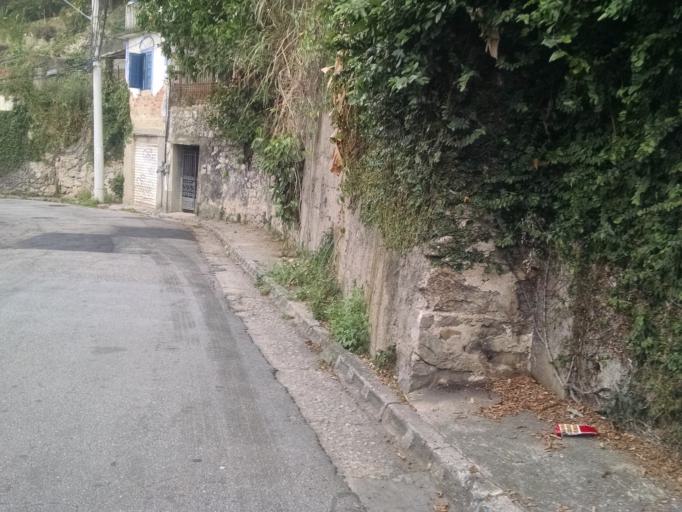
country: BR
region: Rio de Janeiro
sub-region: Rio De Janeiro
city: Rio de Janeiro
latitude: -22.9347
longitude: -43.1953
